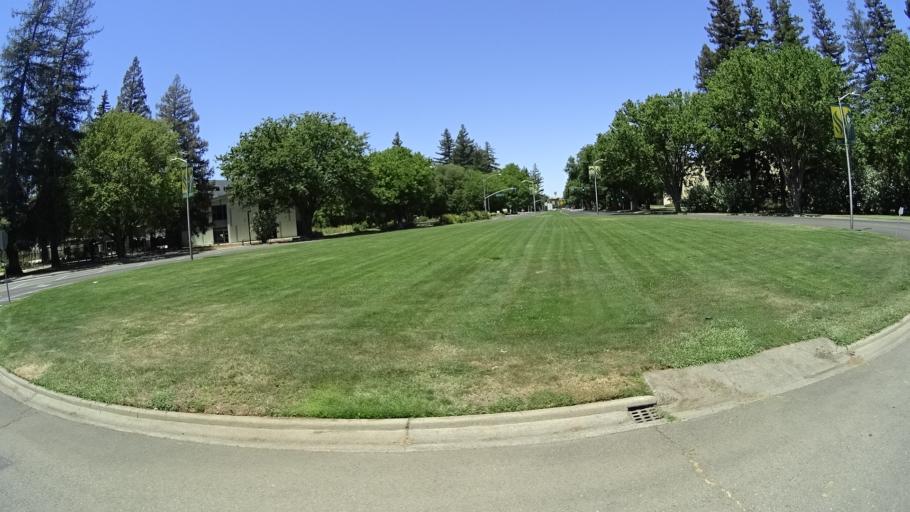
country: US
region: California
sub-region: Sacramento County
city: Arden-Arcade
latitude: 38.5643
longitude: -121.4263
